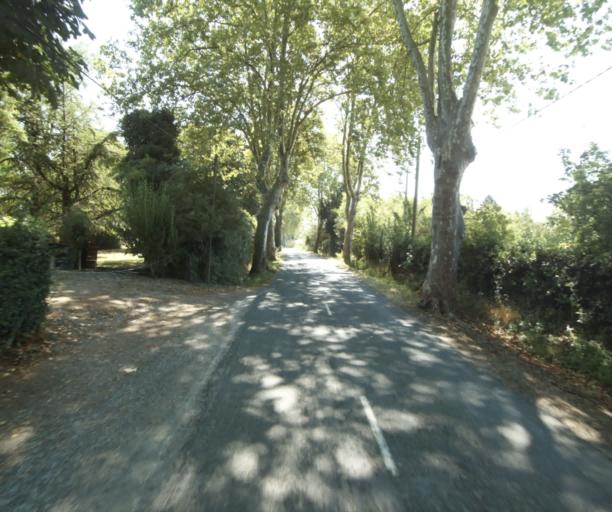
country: FR
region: Midi-Pyrenees
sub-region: Departement de la Haute-Garonne
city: Revel
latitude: 43.5037
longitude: 1.9488
